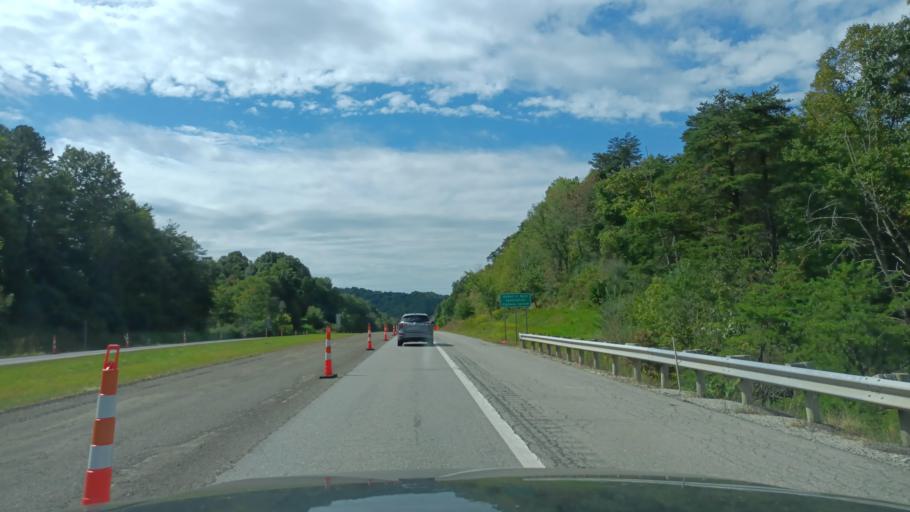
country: US
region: West Virginia
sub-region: Ritchie County
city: Harrisville
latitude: 39.2616
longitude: -81.1301
